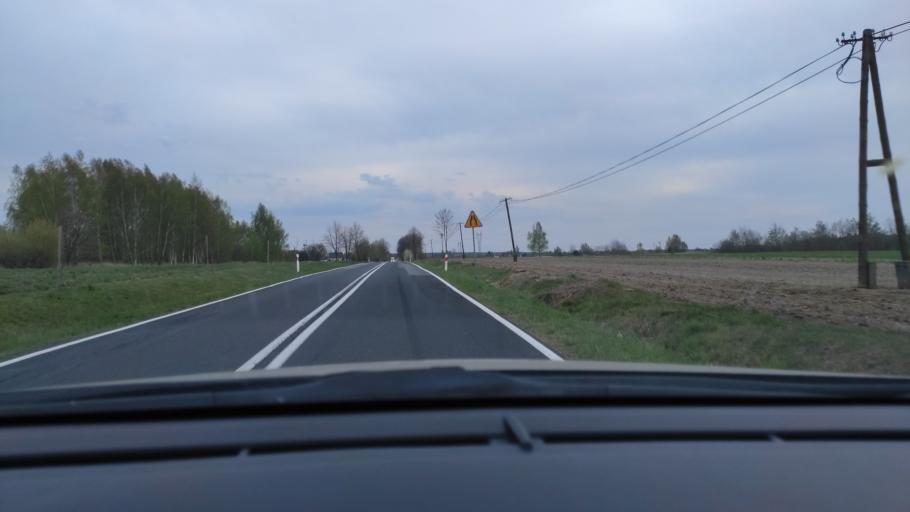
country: PL
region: Masovian Voivodeship
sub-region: Powiat zwolenski
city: Zwolen
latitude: 51.3718
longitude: 21.5634
